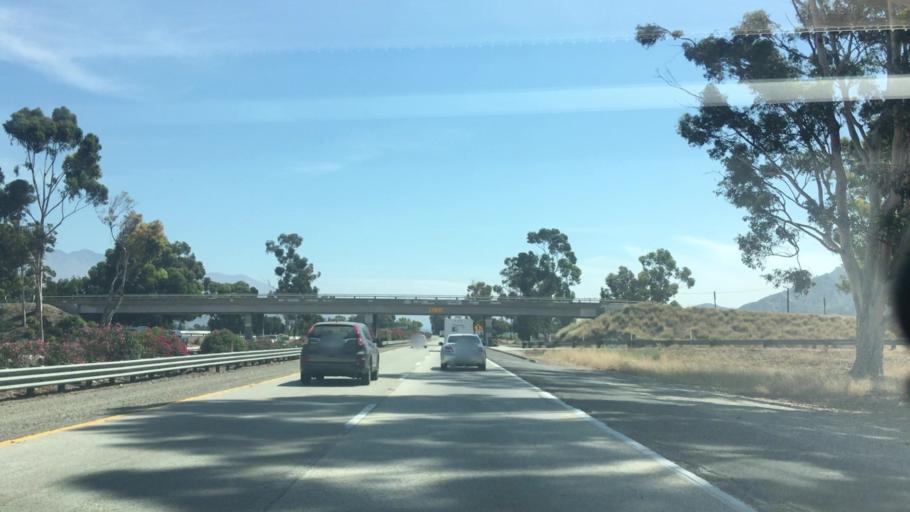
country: US
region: California
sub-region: Ventura County
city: Santa Paula
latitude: 34.3216
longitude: -119.1023
